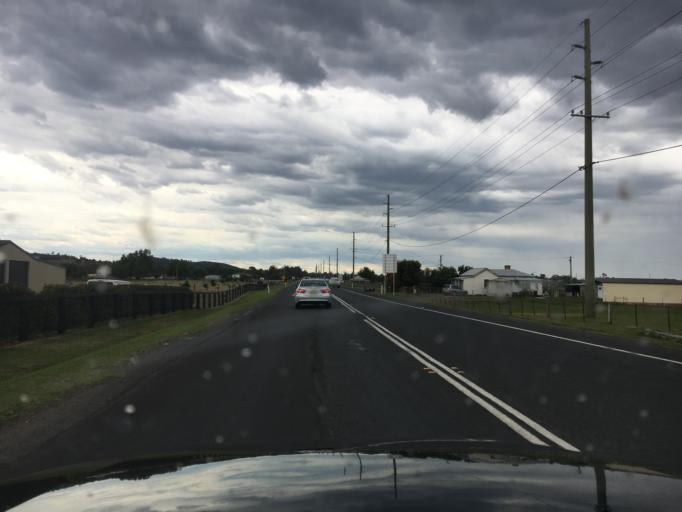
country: AU
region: New South Wales
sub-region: Muswellbrook
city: Muswellbrook
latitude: -32.1461
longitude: 150.8830
